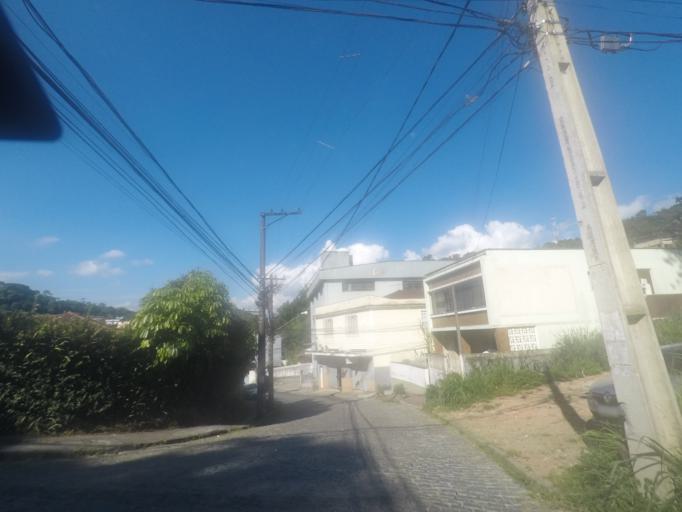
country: BR
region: Rio de Janeiro
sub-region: Petropolis
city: Petropolis
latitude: -22.5384
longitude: -43.2002
